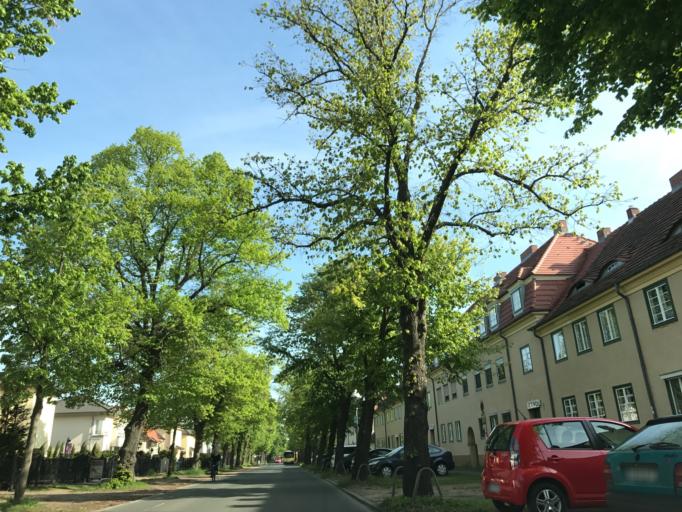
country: DE
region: Berlin
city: Staaken
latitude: 52.5409
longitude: 13.1430
